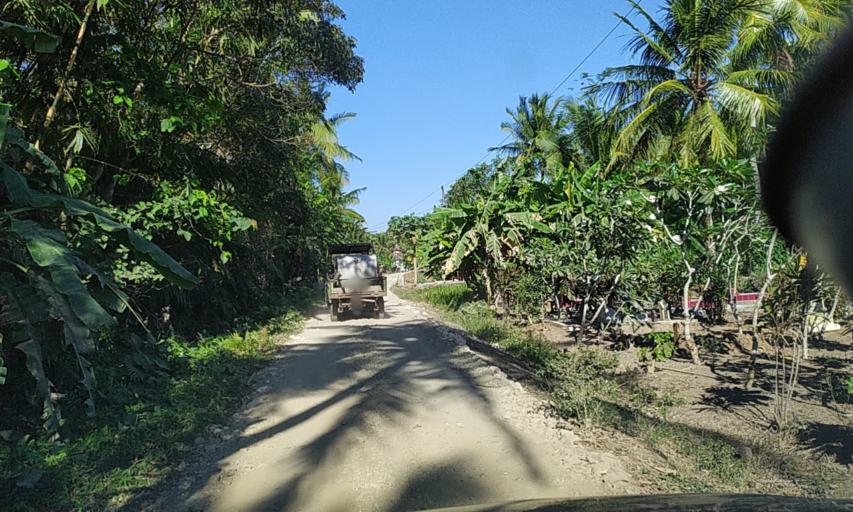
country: ID
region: Central Java
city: Kalenaren
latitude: -7.5911
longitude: 108.7951
